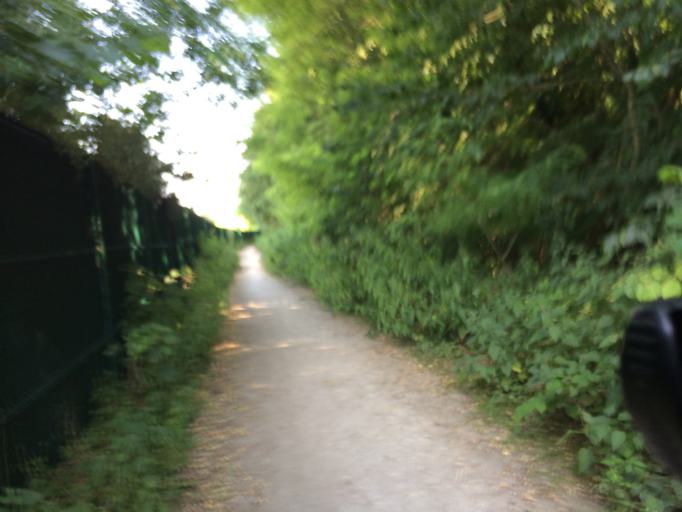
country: FR
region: Ile-de-France
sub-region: Departement de l'Essonne
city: Montgeron
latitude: 48.6877
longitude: 2.4391
